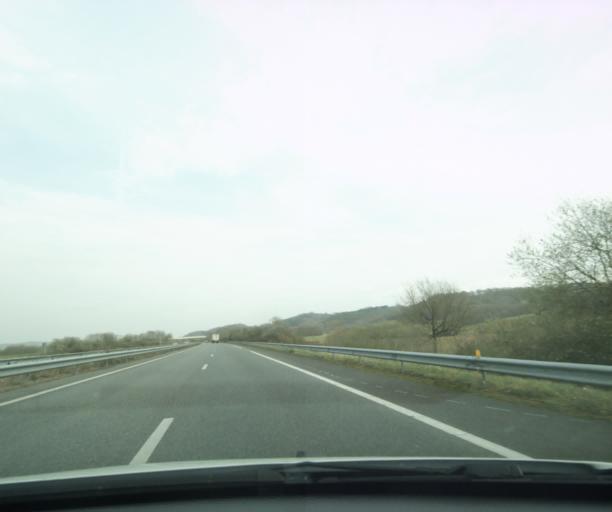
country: FR
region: Aquitaine
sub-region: Departement des Landes
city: Labatut
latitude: 43.5182
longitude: -0.9704
